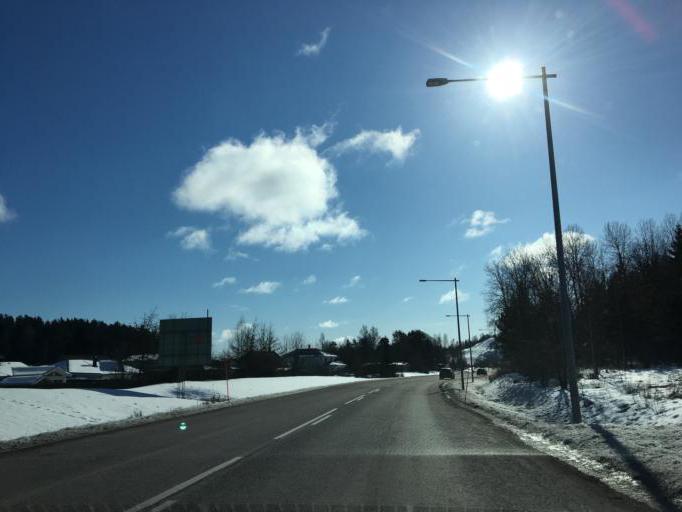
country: SE
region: Vaestmanland
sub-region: Vasteras
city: Vasteras
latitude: 59.6318
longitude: 16.4775
